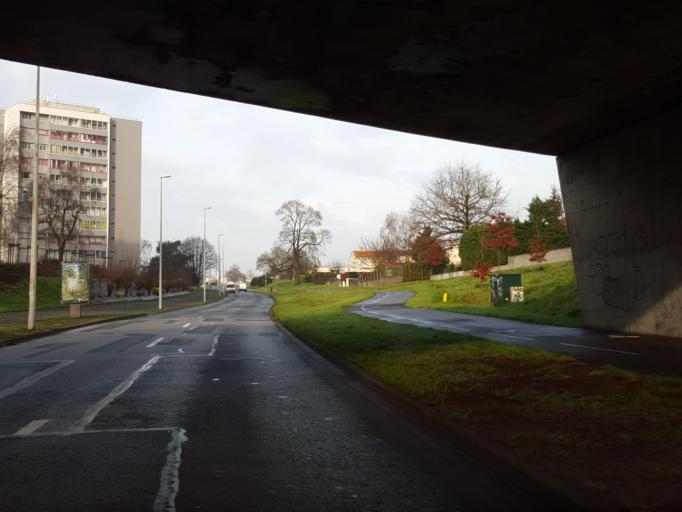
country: FR
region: Pays de la Loire
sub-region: Departement de la Vendee
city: La Roche-sur-Yon
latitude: 46.6809
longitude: -1.4217
